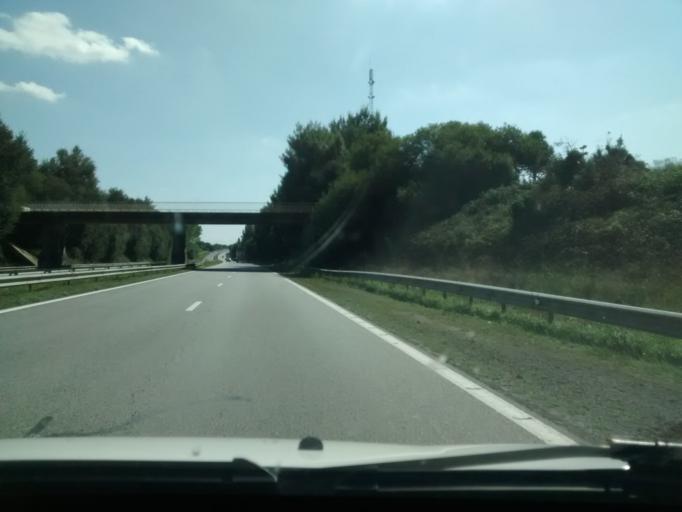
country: FR
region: Brittany
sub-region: Departement d'Ille-et-Vilaine
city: Quedillac
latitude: 48.2520
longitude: -2.1377
